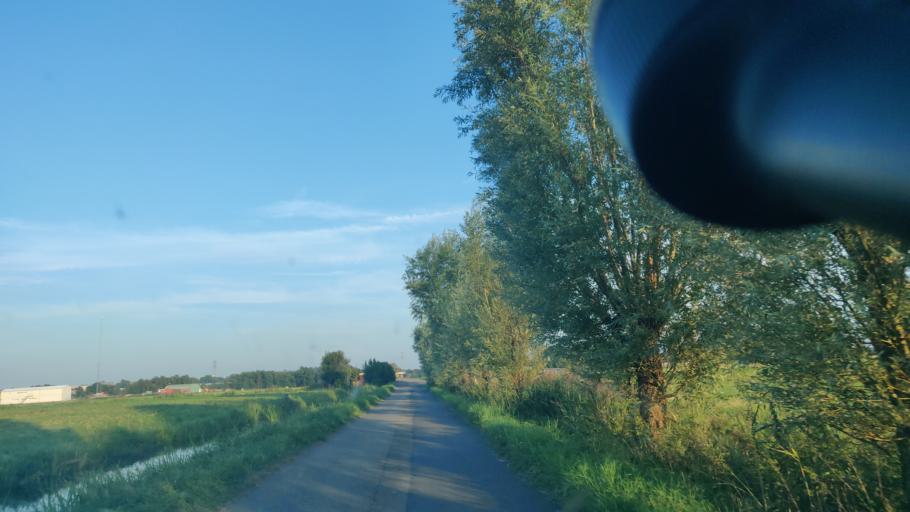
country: NL
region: South Holland
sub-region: Gemeente Voorschoten
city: Voorschoten
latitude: 52.1468
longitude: 4.4360
